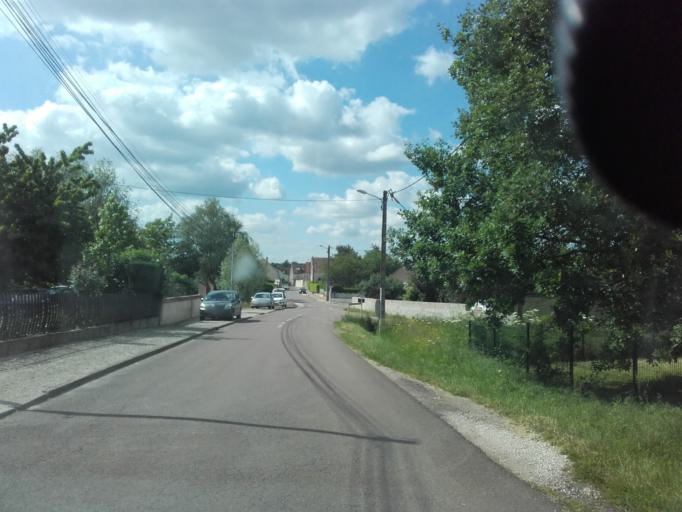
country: FR
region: Bourgogne
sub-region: Departement de Saone-et-Loire
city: Chagny
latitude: 46.8974
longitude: 4.7706
